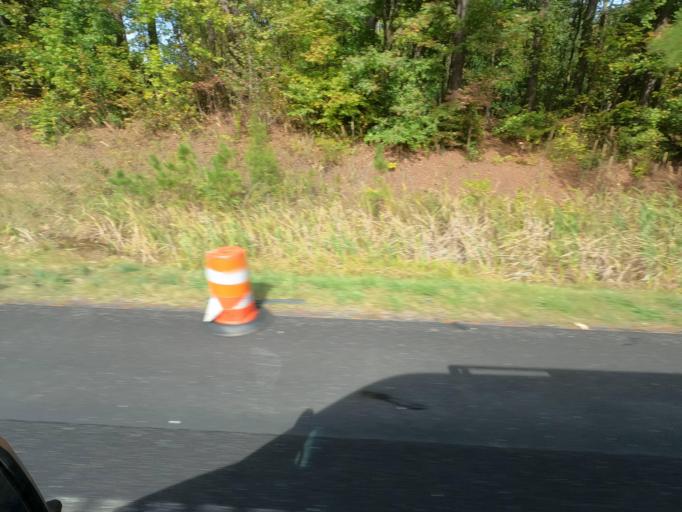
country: US
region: Tennessee
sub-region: Decatur County
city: Parsons
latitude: 35.8237
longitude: -88.1279
